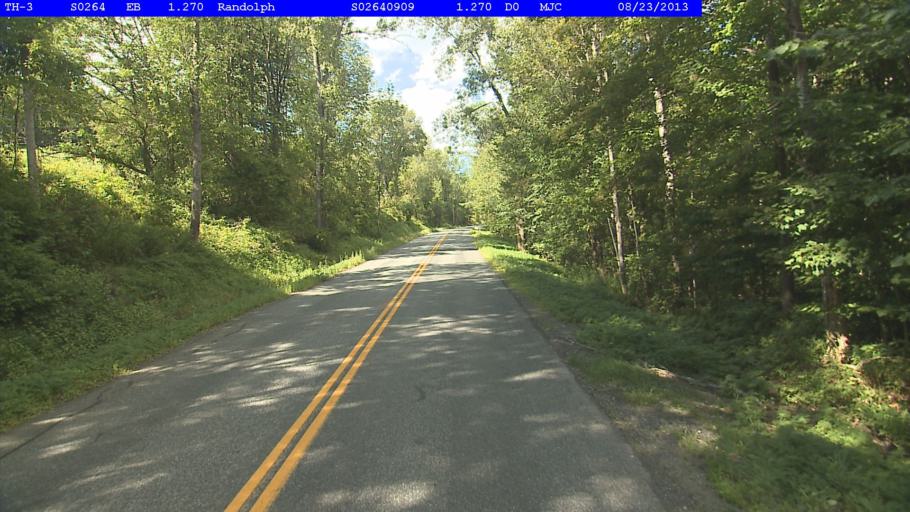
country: US
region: Vermont
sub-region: Orange County
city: Chelsea
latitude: 43.9468
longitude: -72.5384
